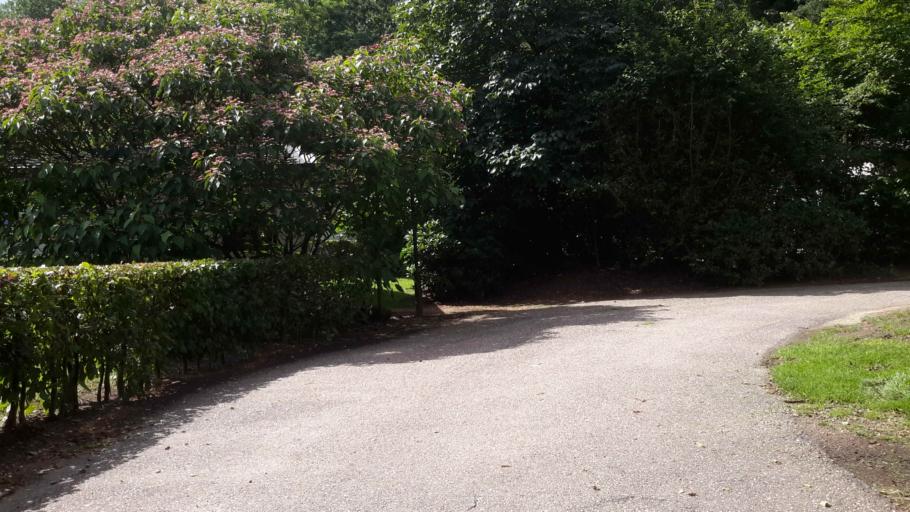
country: NL
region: Gelderland
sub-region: Gemeente Epe
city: Epe
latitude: 52.3462
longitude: 5.9422
